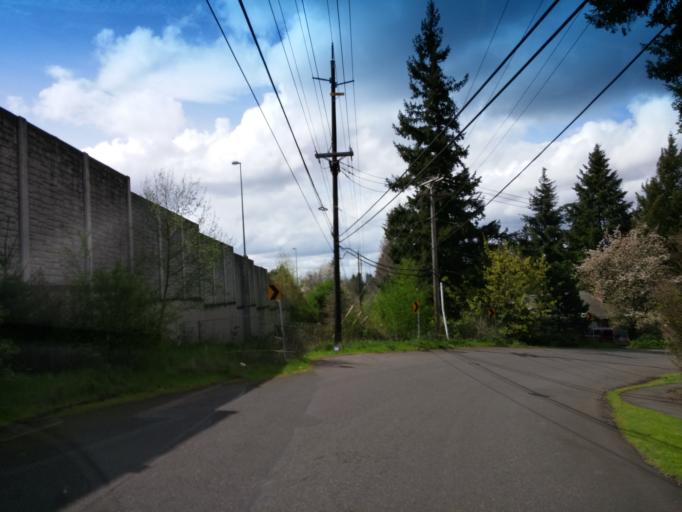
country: US
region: Oregon
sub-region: Washington County
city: Cedar Hills
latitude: 45.5168
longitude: -122.8002
